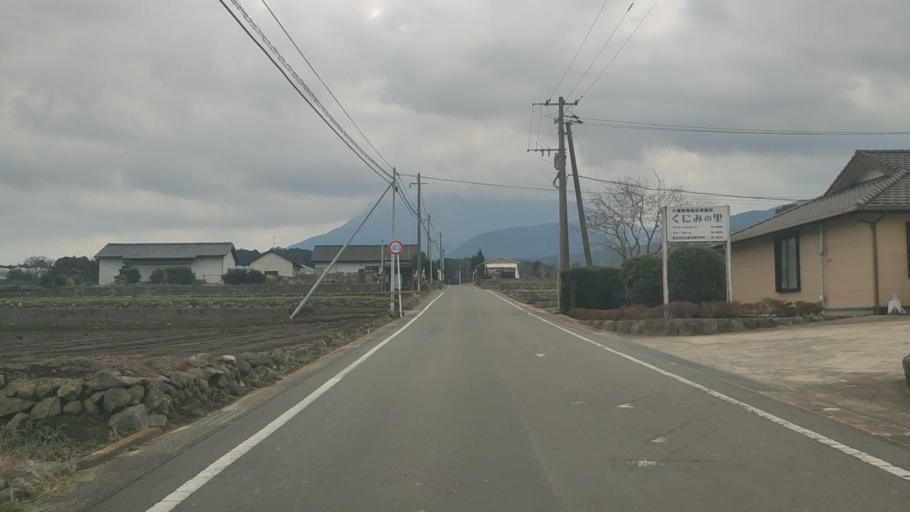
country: JP
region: Nagasaki
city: Shimabara
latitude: 32.8311
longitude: 130.2917
